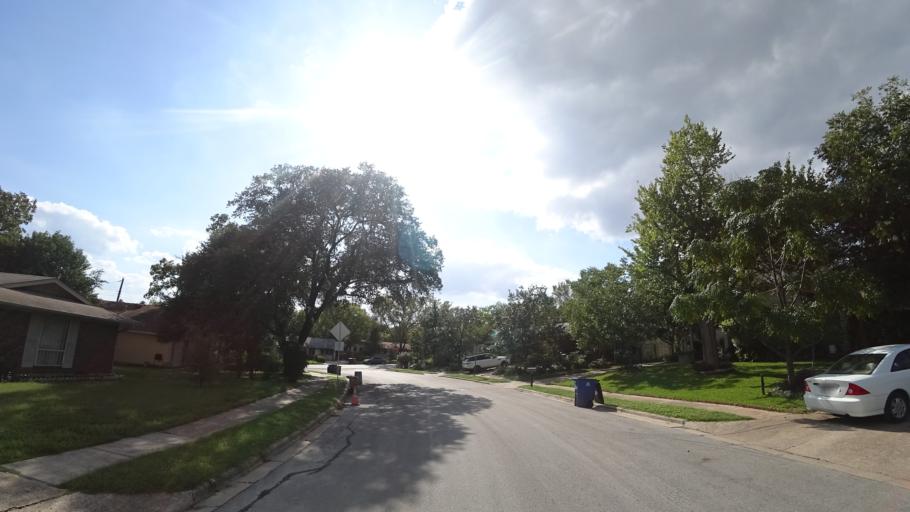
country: US
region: Texas
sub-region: Travis County
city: Wells Branch
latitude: 30.3574
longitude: -97.7039
